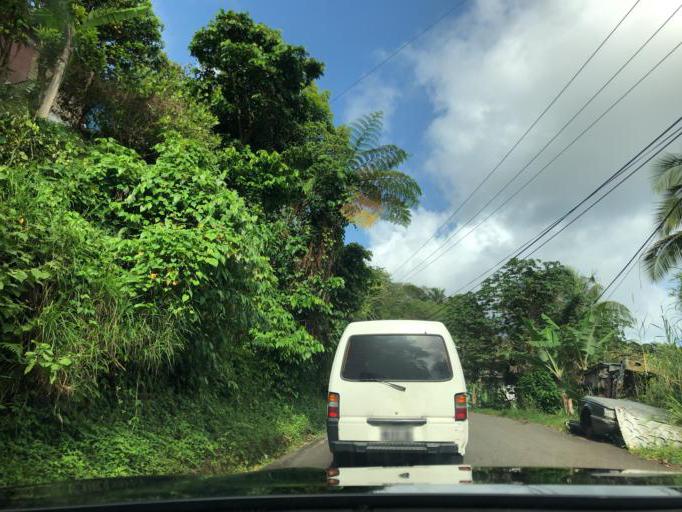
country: LC
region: Castries Quarter
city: Bisee
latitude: 13.9899
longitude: -60.9604
